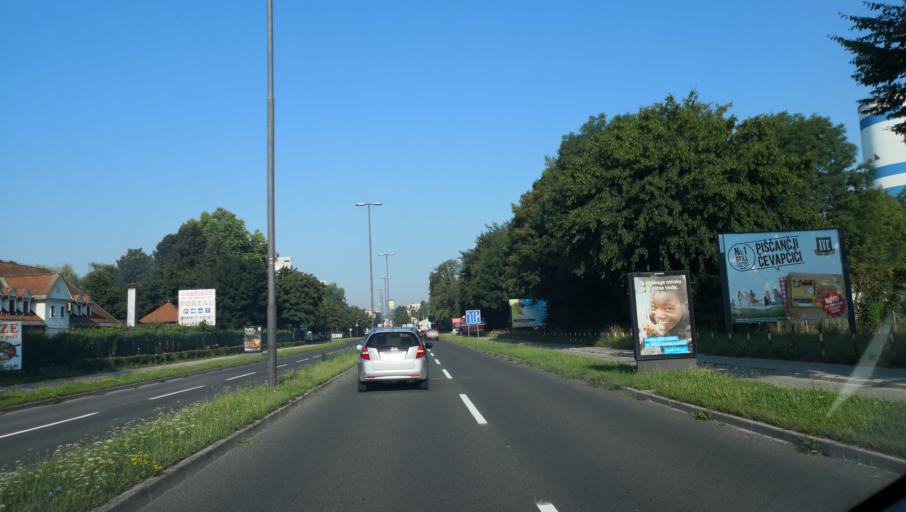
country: SI
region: Ljubljana
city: Ljubljana
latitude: 46.0561
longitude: 14.5477
